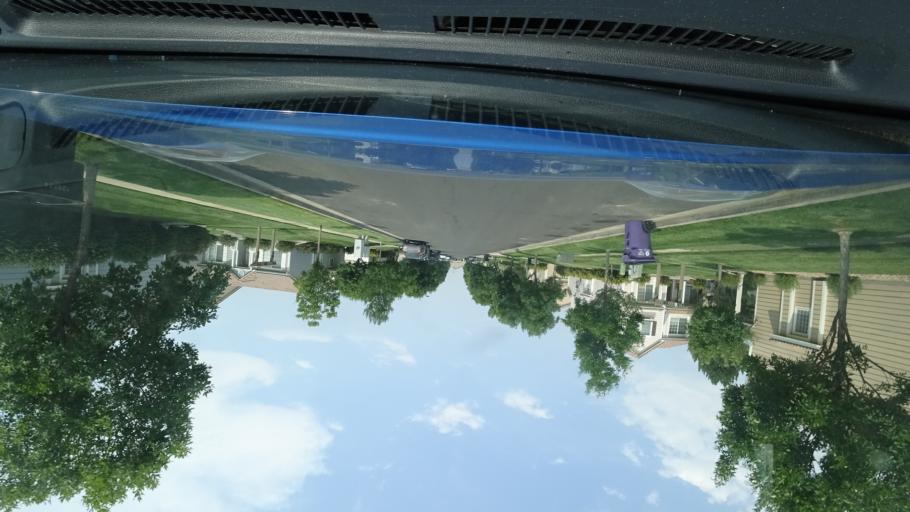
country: US
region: Colorado
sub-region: Adams County
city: Aurora
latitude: 39.7799
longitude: -104.7382
